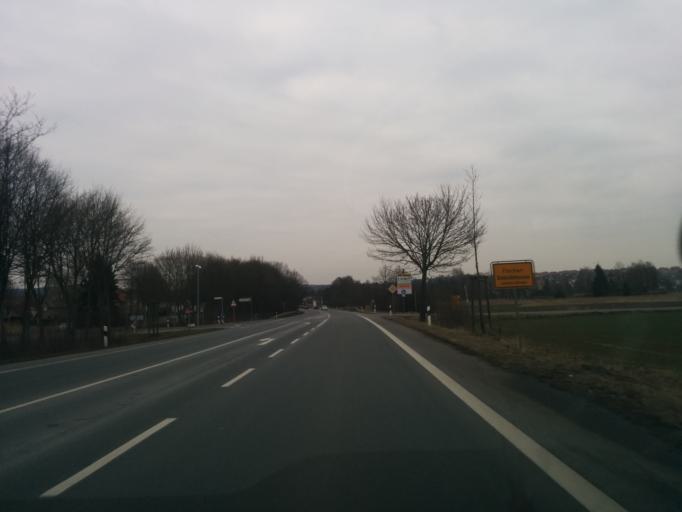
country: DE
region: Lower Saxony
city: Gieboldehausen
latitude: 51.6014
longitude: 10.2056
